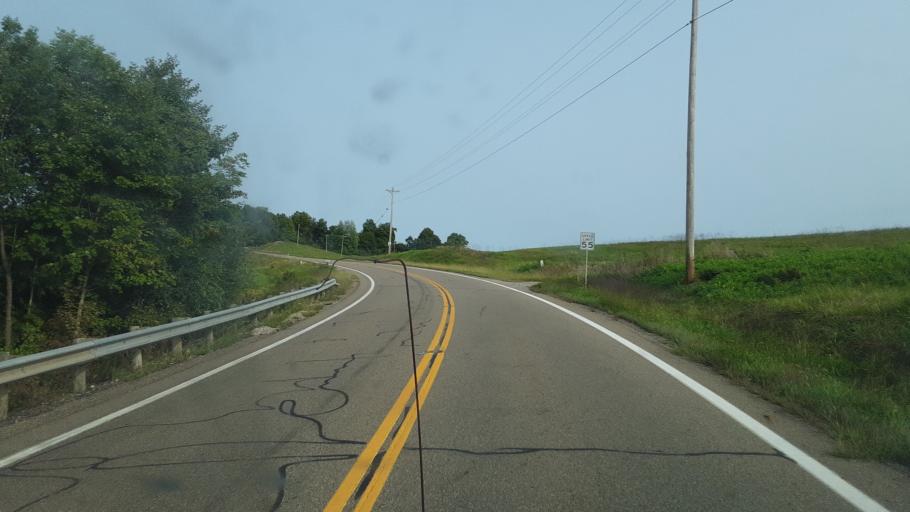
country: US
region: Ohio
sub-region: Coshocton County
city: Coshocton
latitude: 40.4093
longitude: -81.8818
